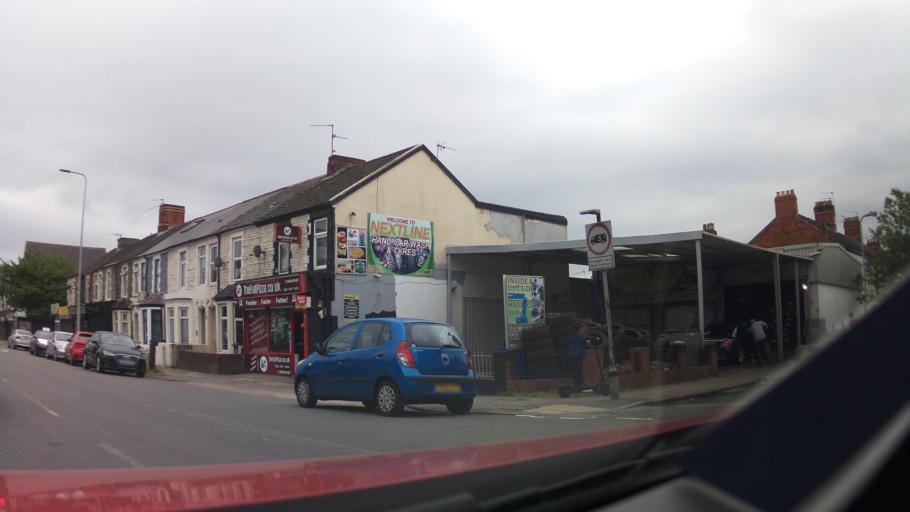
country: GB
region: Wales
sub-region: Cardiff
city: Cardiff
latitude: 51.4719
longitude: -3.1866
